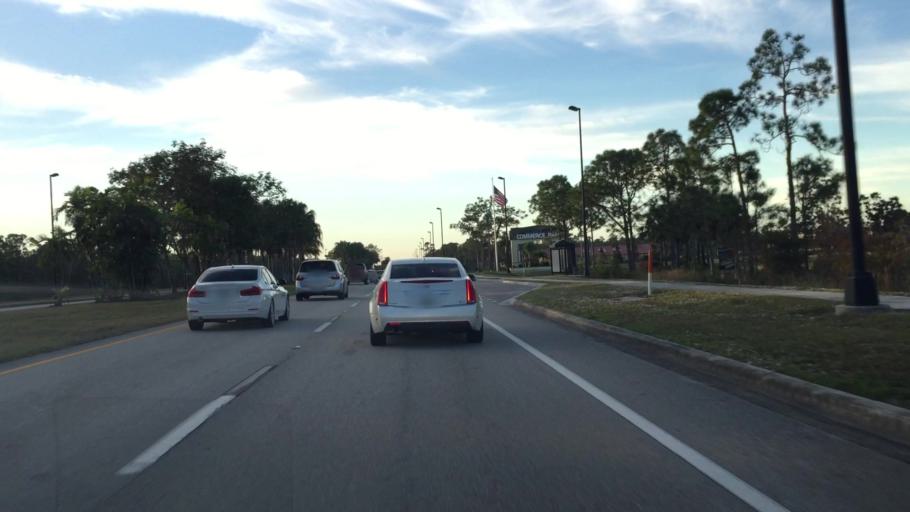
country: US
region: Florida
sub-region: Lee County
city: Gateway
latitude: 26.5311
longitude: -81.7858
